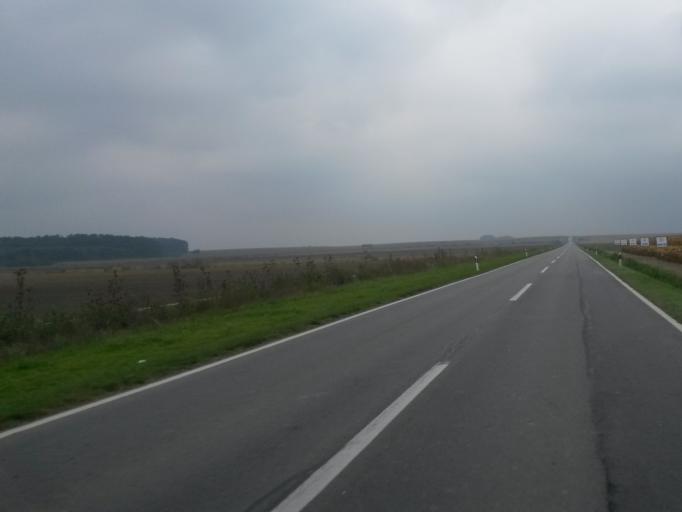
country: HR
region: Osjecko-Baranjska
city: Viskovci
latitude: 45.3920
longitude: 18.4543
